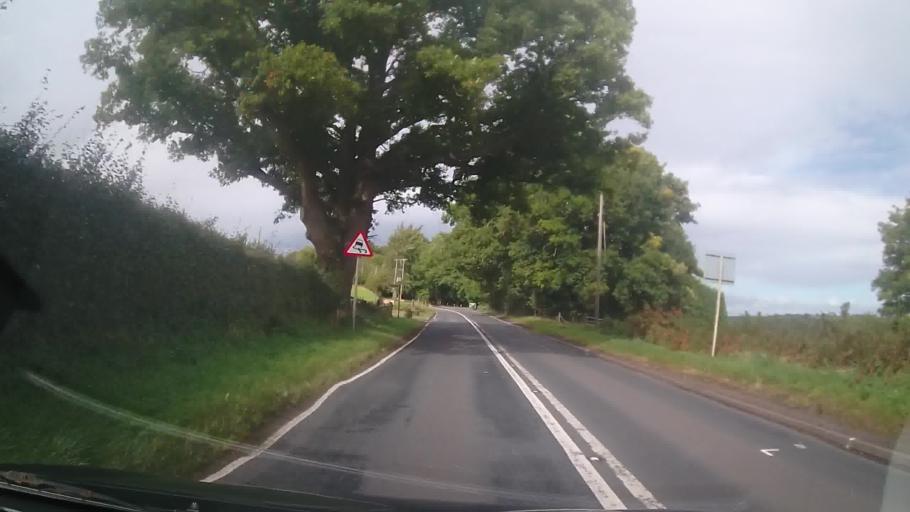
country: GB
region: England
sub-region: Shropshire
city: Romsley
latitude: 52.4240
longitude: -2.2987
